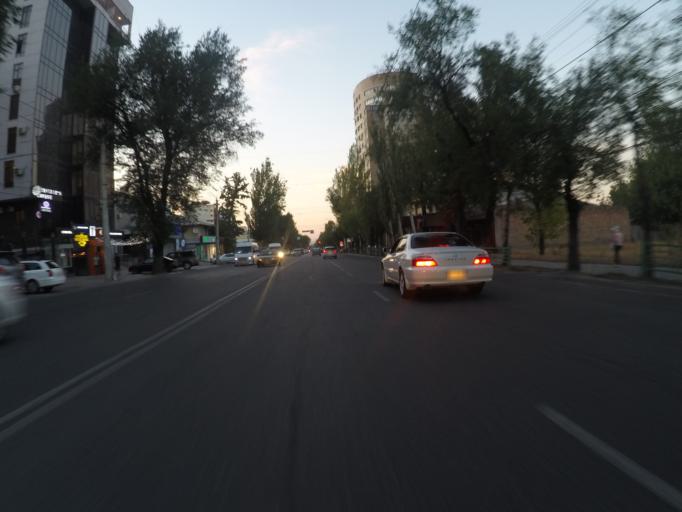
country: KG
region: Chuy
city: Bishkek
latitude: 42.8540
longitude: 74.6100
